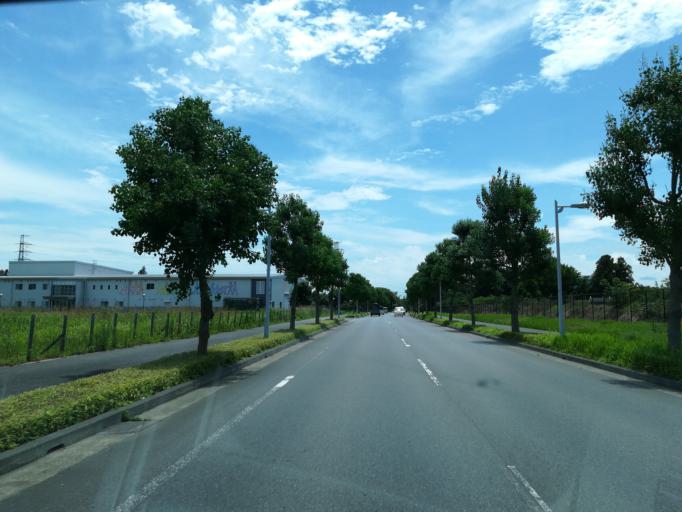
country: JP
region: Ibaraki
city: Naka
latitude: 36.0756
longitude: 140.0796
